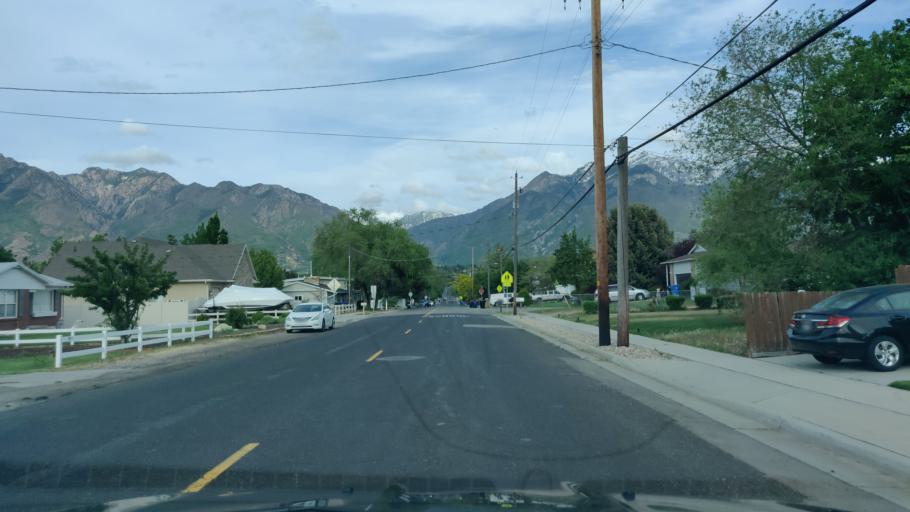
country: US
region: Utah
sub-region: Salt Lake County
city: Little Cottonwood Creek Valley
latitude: 40.6204
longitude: -111.8451
